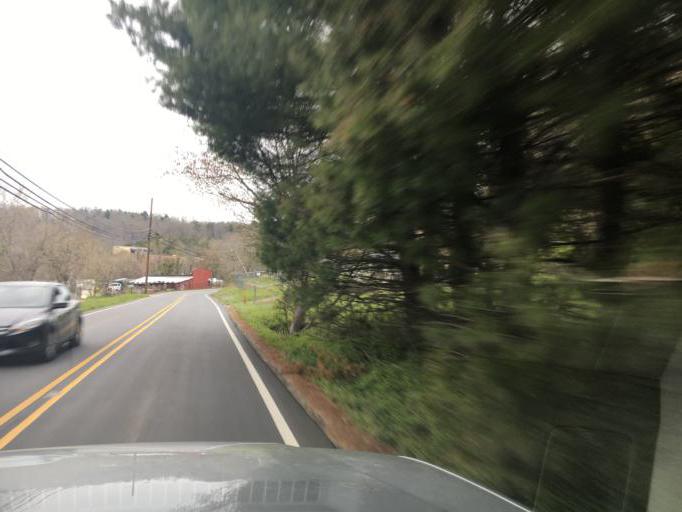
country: US
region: North Carolina
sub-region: Buncombe County
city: Woodfin
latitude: 35.6259
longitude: -82.5996
